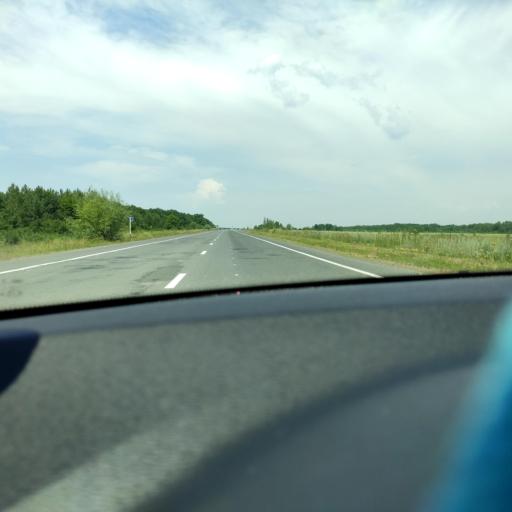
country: RU
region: Samara
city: Petra-Dubrava
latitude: 53.3264
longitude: 50.4275
